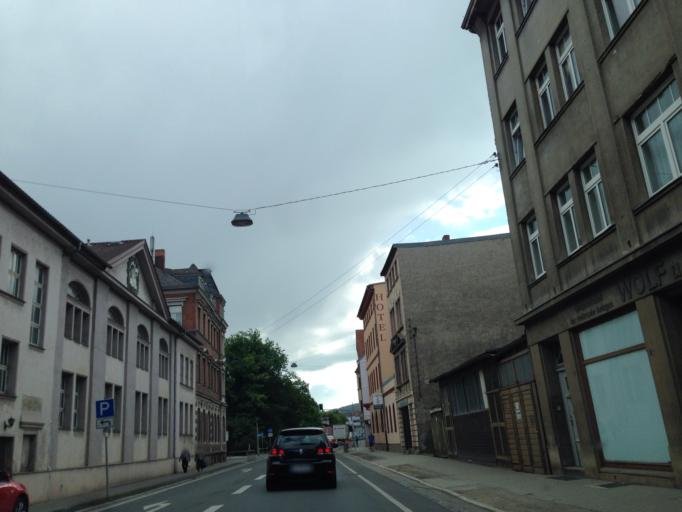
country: DE
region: Thuringia
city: Rudolstadt
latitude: 50.7192
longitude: 11.3406
